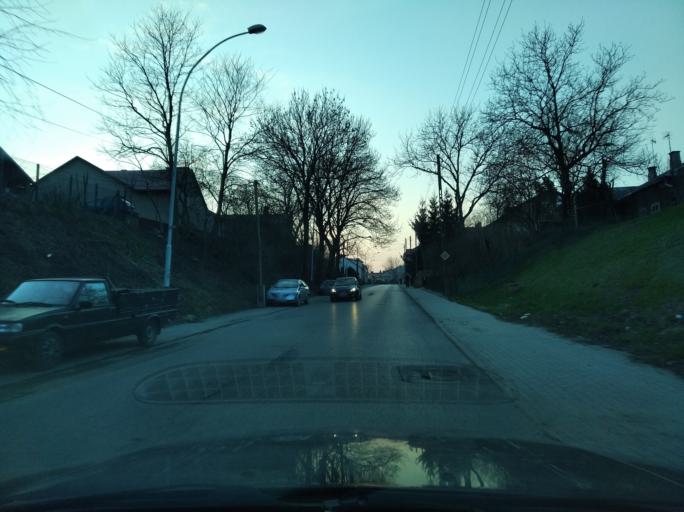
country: PL
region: Subcarpathian Voivodeship
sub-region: Powiat przeworski
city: Przeworsk
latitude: 50.0564
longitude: 22.4984
